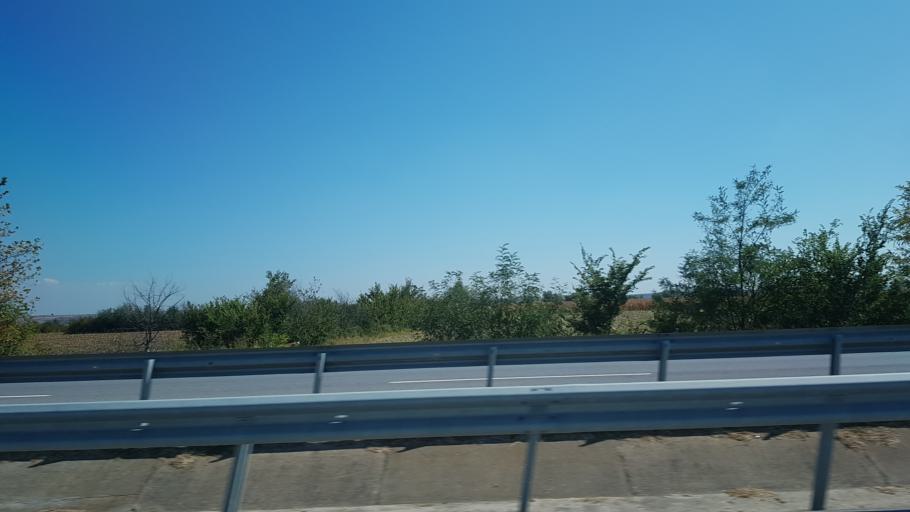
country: TR
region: Kirklareli
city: Inece
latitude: 41.5722
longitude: 27.1477
